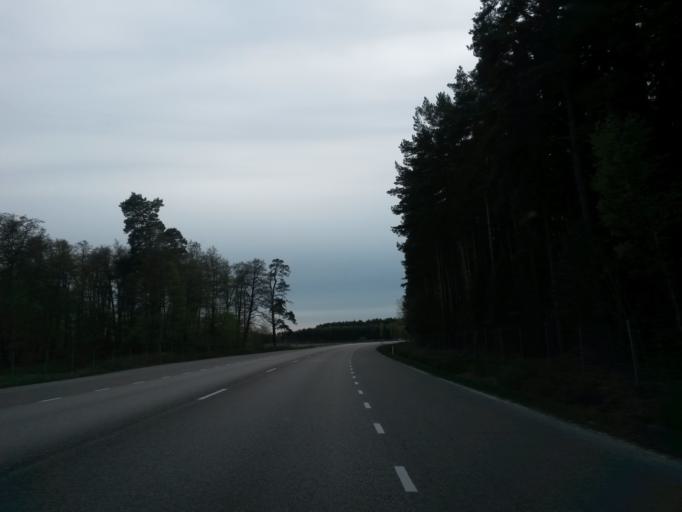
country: SE
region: Vaestra Goetaland
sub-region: Vara Kommun
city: Vara
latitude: 58.2271
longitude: 12.9240
